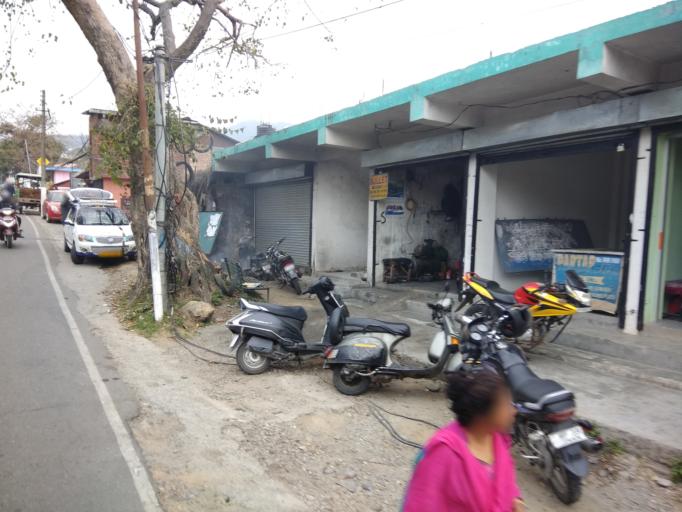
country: IN
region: Himachal Pradesh
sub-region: Kangra
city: Dharmsala
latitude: 32.2096
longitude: 76.3225
